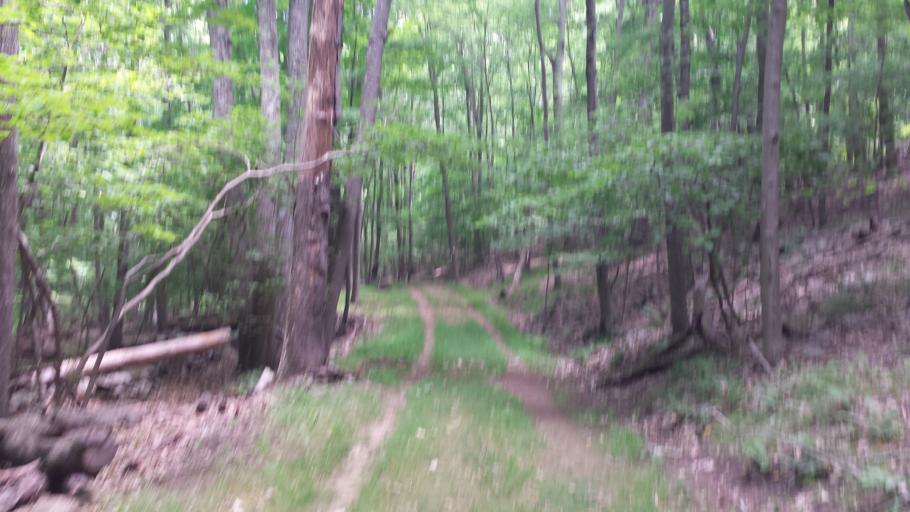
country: US
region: Connecticut
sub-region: Fairfield County
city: Ridgefield
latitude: 41.3059
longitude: -73.5570
